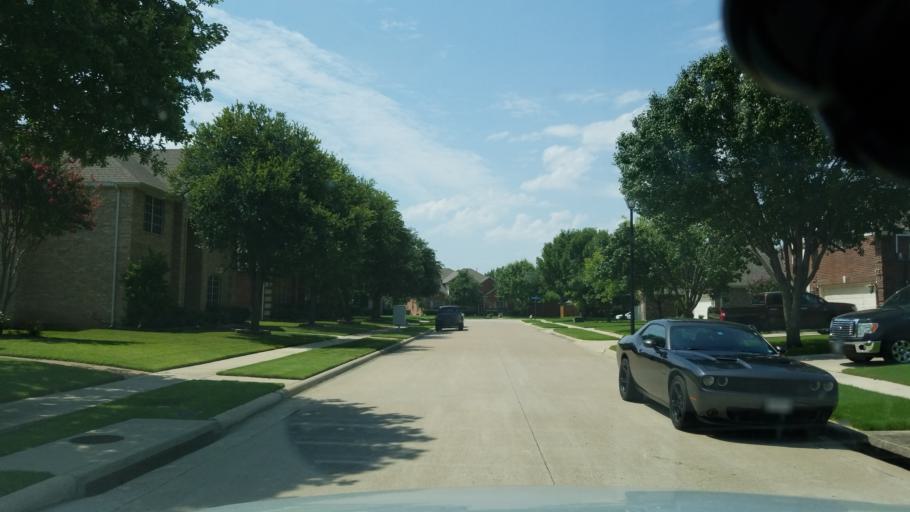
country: US
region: Texas
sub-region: Dallas County
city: Coppell
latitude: 32.9667
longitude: -96.9874
